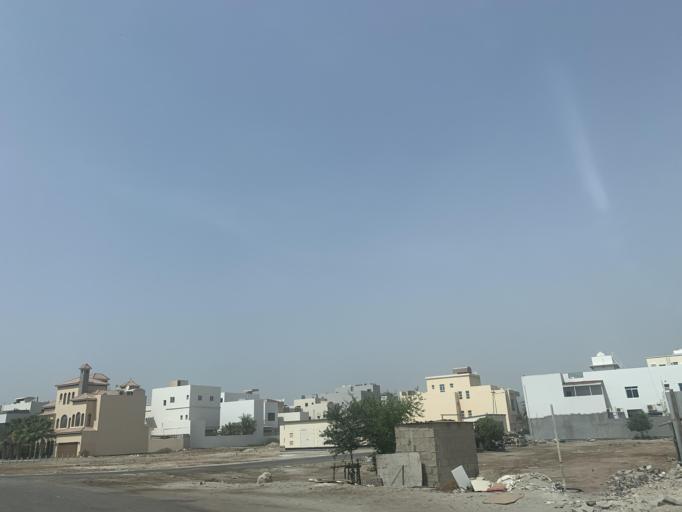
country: BH
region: Northern
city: Madinat `Isa
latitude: 26.1936
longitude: 50.4900
